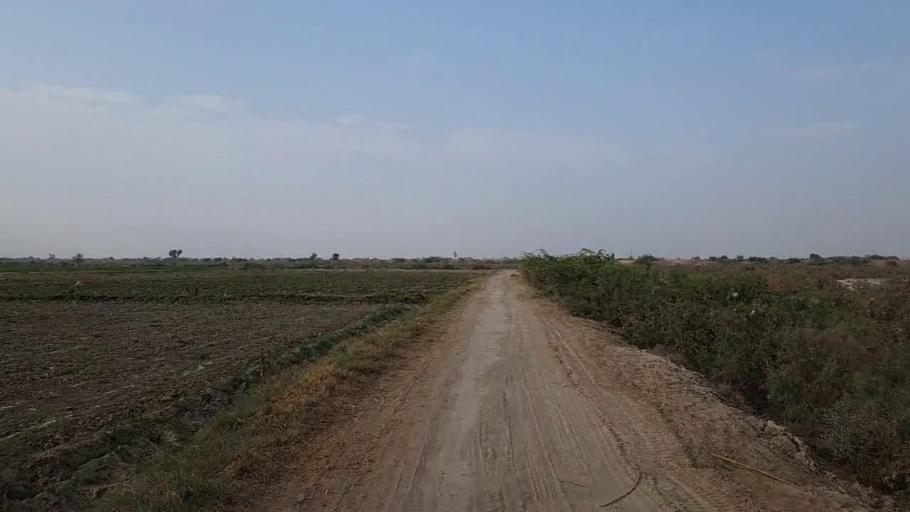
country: PK
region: Sindh
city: Pithoro
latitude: 25.4374
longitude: 69.2370
